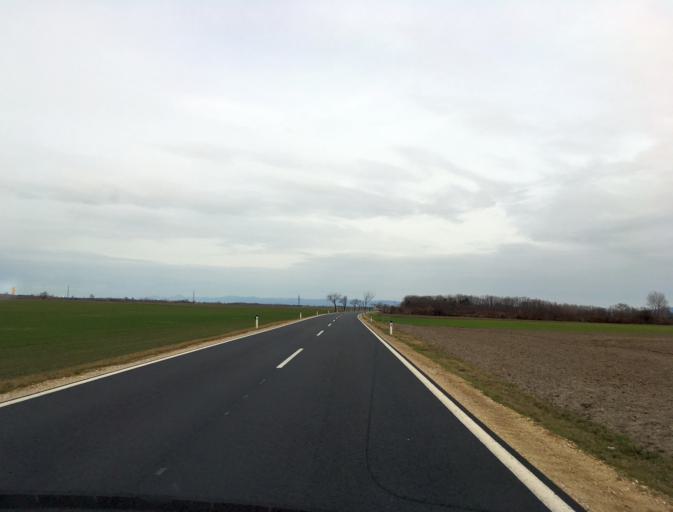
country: AT
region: Lower Austria
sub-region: Politischer Bezirk Ganserndorf
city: Haringsee
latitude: 48.2236
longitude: 16.7708
